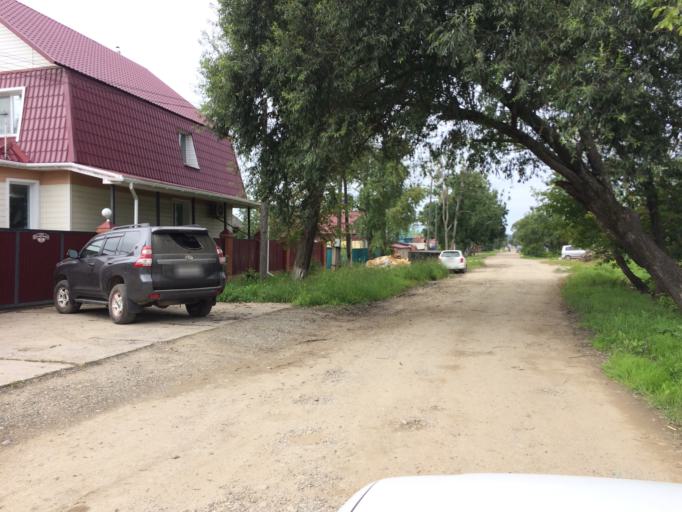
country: RU
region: Primorskiy
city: Dal'nerechensk
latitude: 45.9333
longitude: 133.7417
